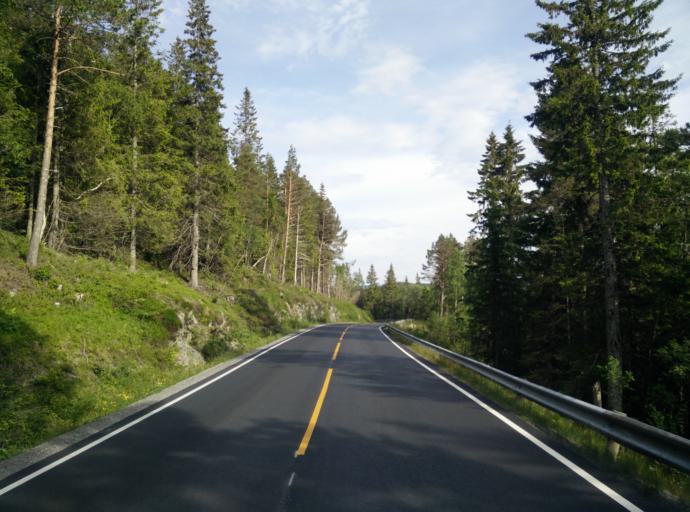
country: NO
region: Sor-Trondelag
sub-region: Snillfjord
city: Krokstadora
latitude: 63.2313
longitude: 9.5652
